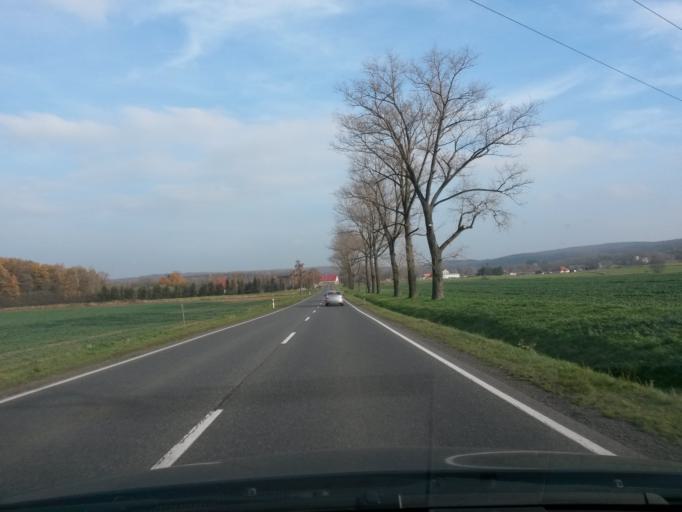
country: PL
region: Lower Silesian Voivodeship
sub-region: Powiat jaworski
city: Bolkow
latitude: 50.9109
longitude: 16.1511
